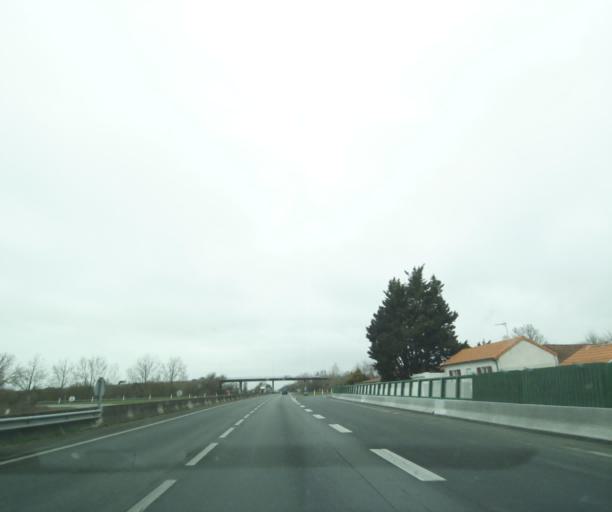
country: FR
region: Poitou-Charentes
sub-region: Departement de la Charente-Maritime
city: Chatelaillon-Plage
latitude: 46.0810
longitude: -1.0768
